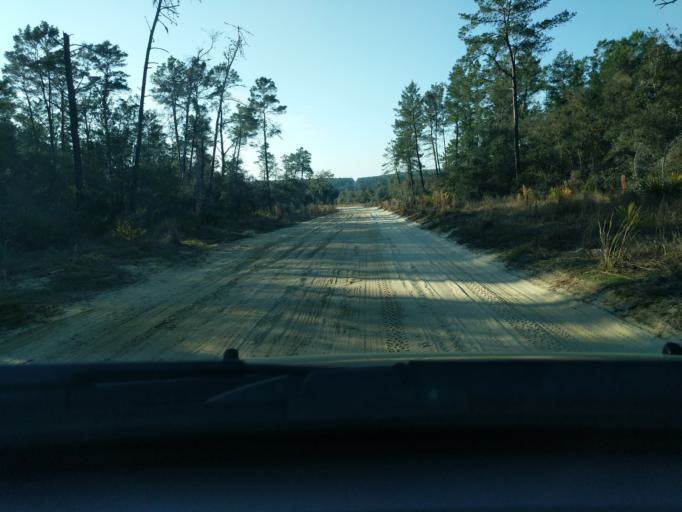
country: US
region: Florida
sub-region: Marion County
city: Silver Springs Shores
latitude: 29.2207
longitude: -81.8276
